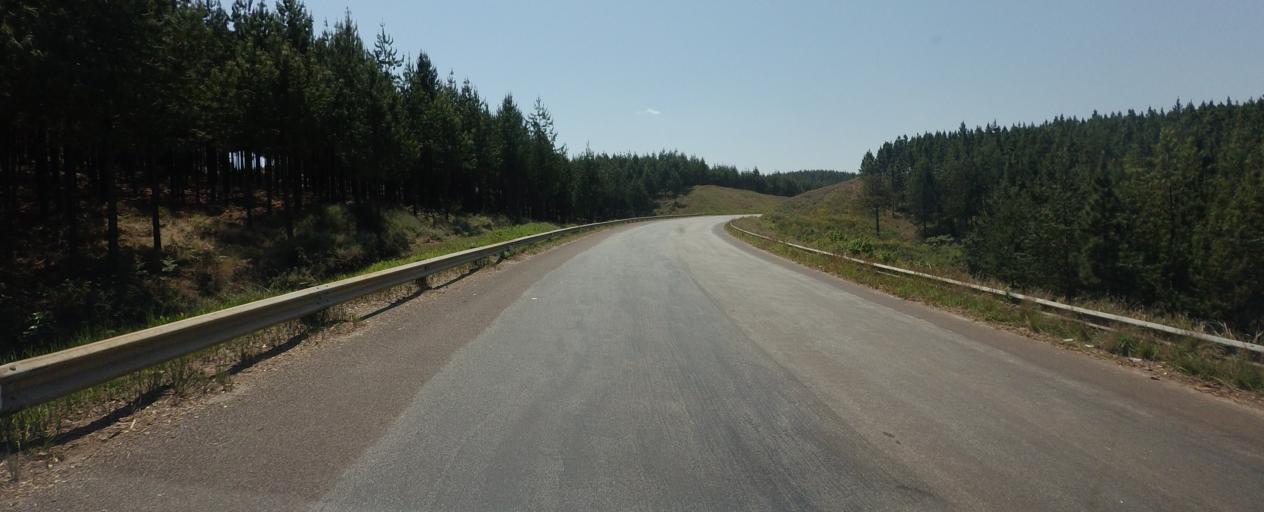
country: ZA
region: Mpumalanga
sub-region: Ehlanzeni District
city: Graksop
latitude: -24.9113
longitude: 30.8419
